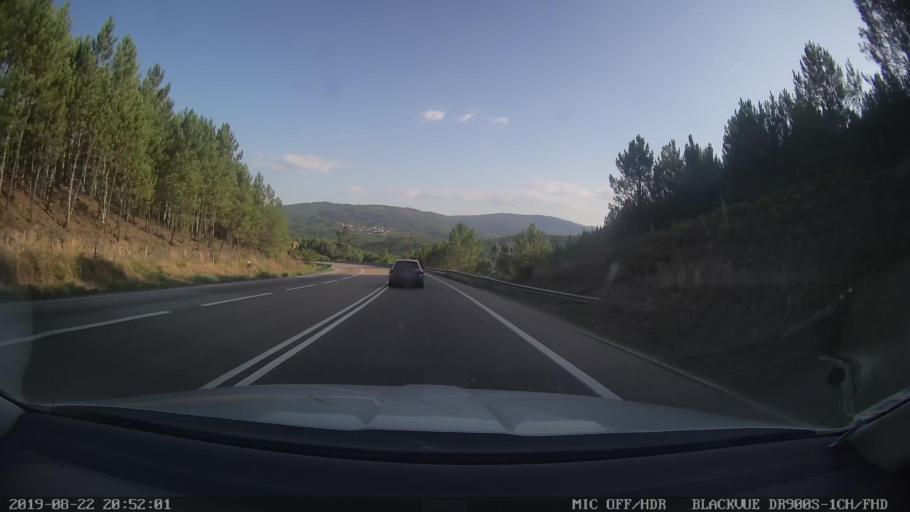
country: PT
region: Castelo Branco
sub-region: Proenca-A-Nova
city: Proenca-a-Nova
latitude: 39.7657
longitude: -7.9668
